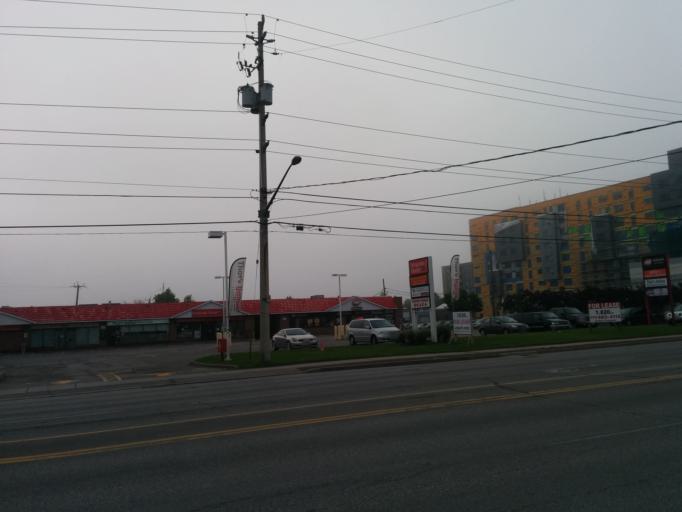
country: CA
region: Ontario
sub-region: York
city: Richmond Hill
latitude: 43.8824
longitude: -79.4400
